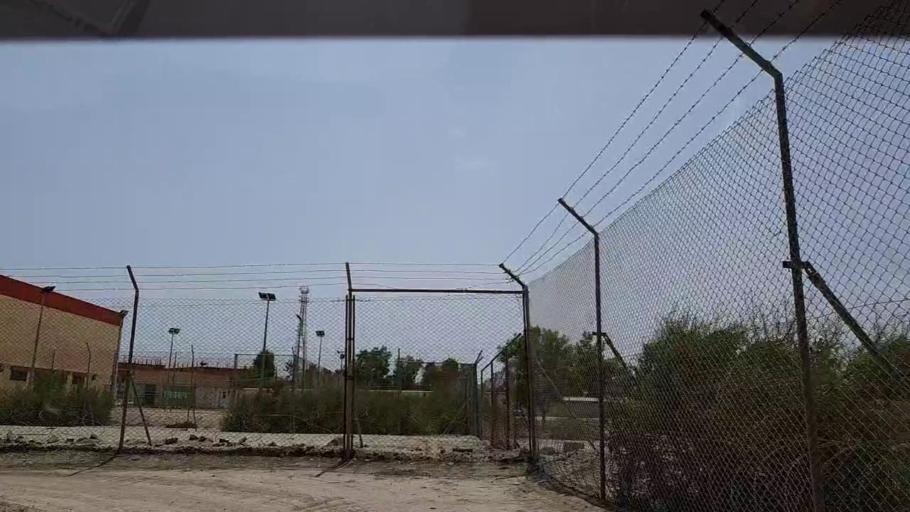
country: PK
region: Sindh
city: Johi
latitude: 26.7085
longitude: 67.6680
